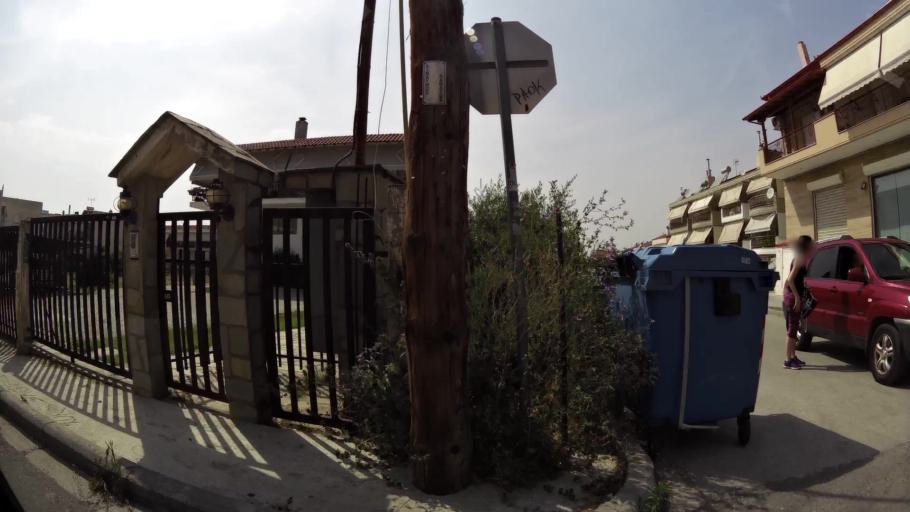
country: GR
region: Central Macedonia
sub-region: Nomos Thessalonikis
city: Efkarpia
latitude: 40.6837
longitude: 22.9467
